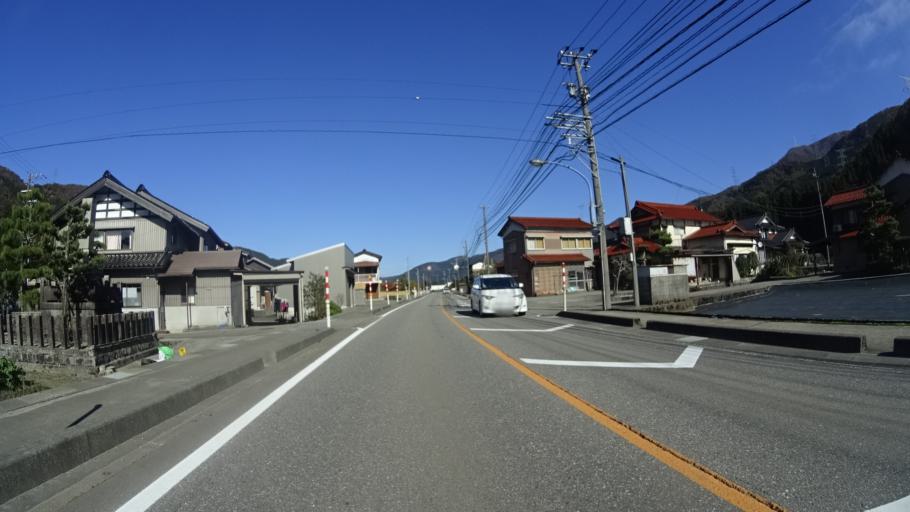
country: JP
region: Ishikawa
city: Tsurugi-asahimachi
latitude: 36.4128
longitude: 136.6320
